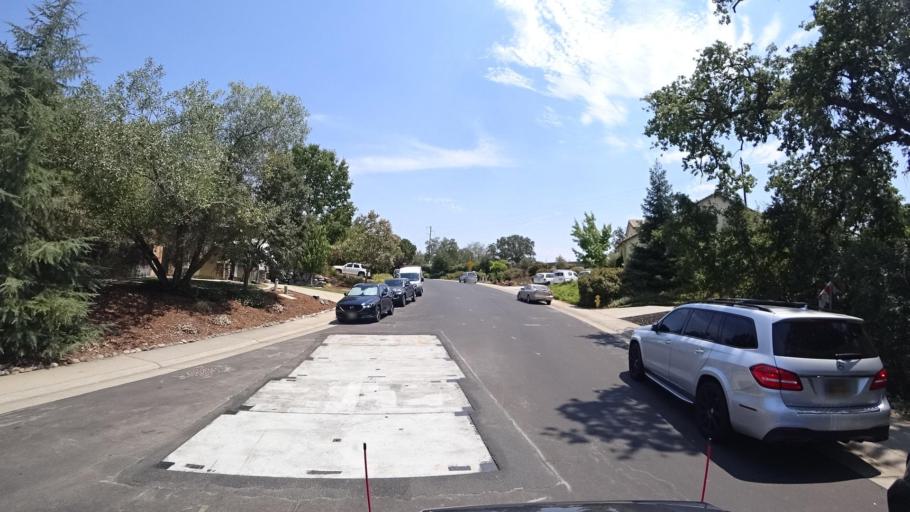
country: US
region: California
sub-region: Placer County
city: Rocklin
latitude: 38.8017
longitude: -121.2267
